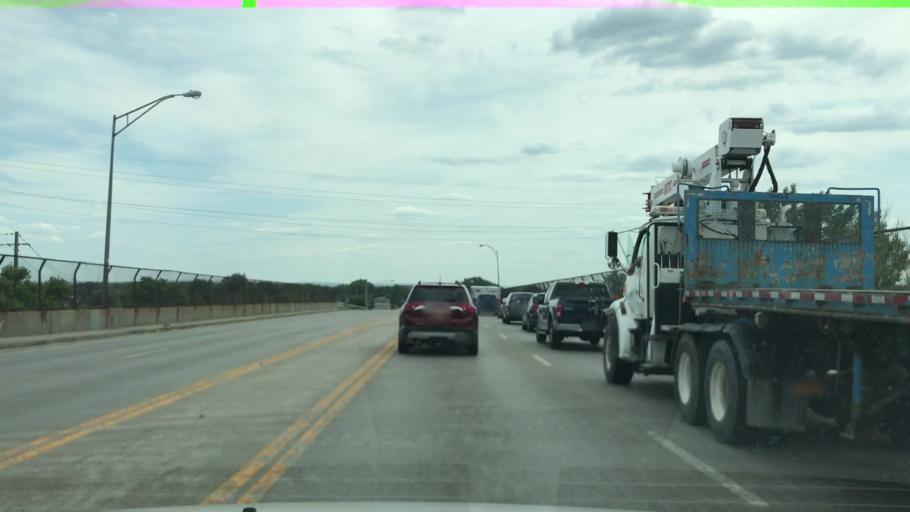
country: US
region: New York
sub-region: Erie County
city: Sloan
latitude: 42.8893
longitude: -78.7848
